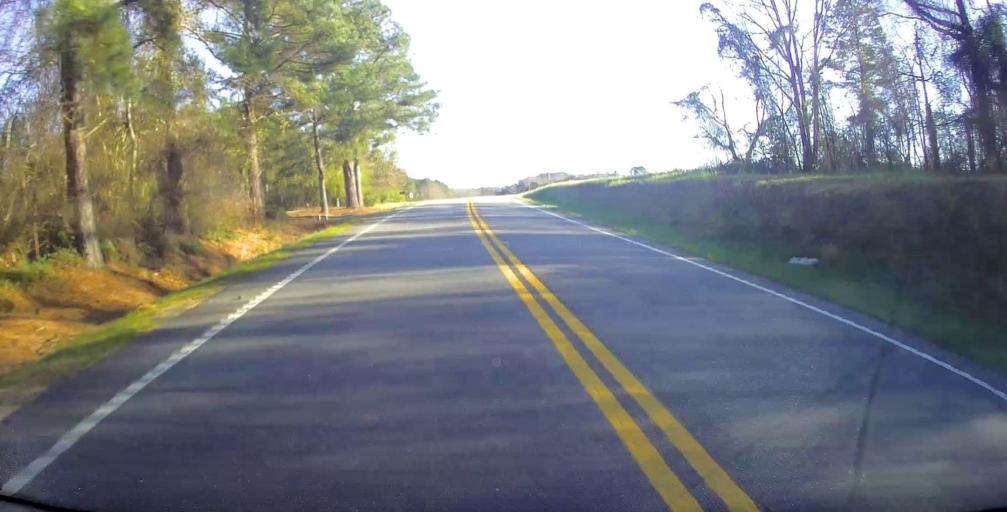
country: US
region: Georgia
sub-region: Taylor County
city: Butler
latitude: 32.4890
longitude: -84.3981
